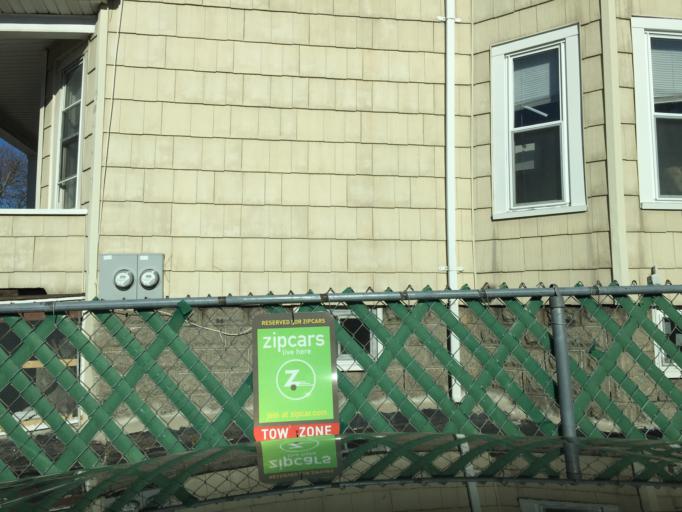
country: US
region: Massachusetts
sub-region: Middlesex County
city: Somerville
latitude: 42.3874
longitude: -71.0812
